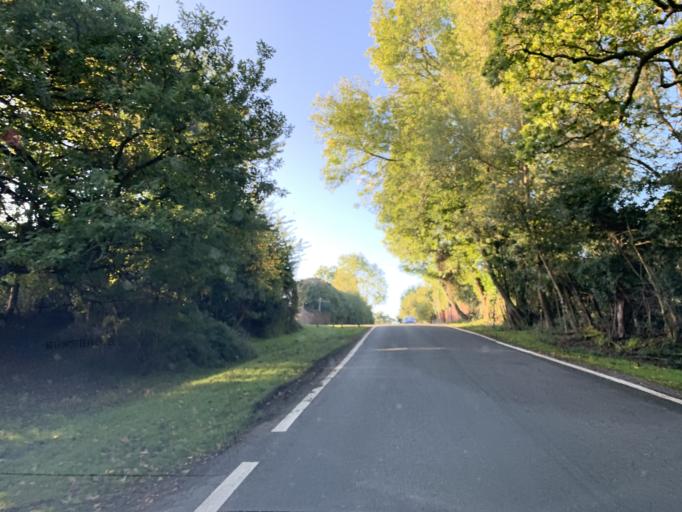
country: GB
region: England
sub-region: Hampshire
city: Cadnam
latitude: 50.9406
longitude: -1.6180
